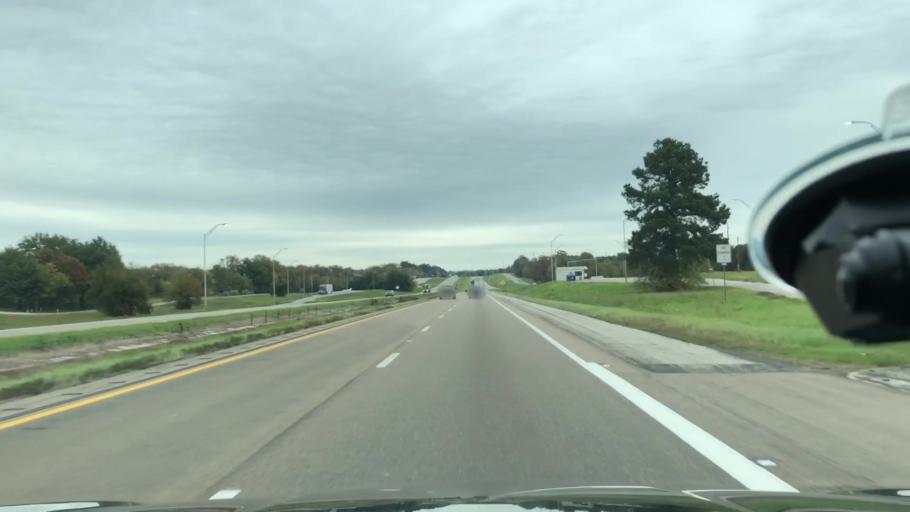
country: US
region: Texas
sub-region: Titus County
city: Mount Pleasant
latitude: 33.1587
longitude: -95.0525
